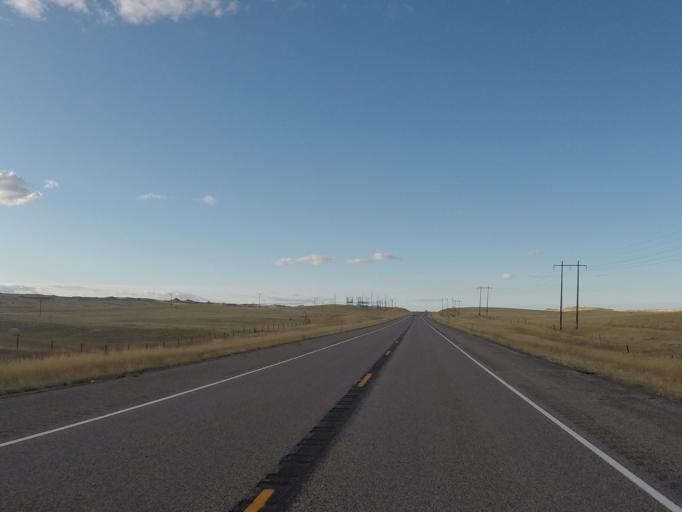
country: US
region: Montana
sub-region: Golden Valley County
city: Ryegate
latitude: 46.2108
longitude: -108.9232
